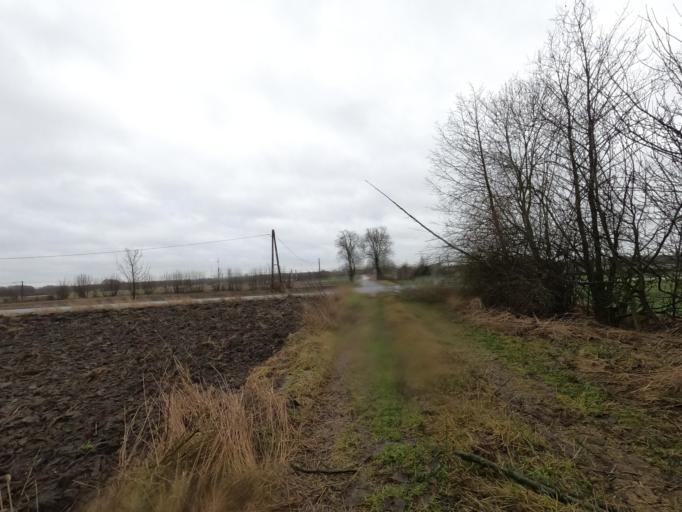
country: PL
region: Greater Poland Voivodeship
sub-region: Powiat pilski
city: Osiek nad Notecia
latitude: 53.1154
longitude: 17.2619
